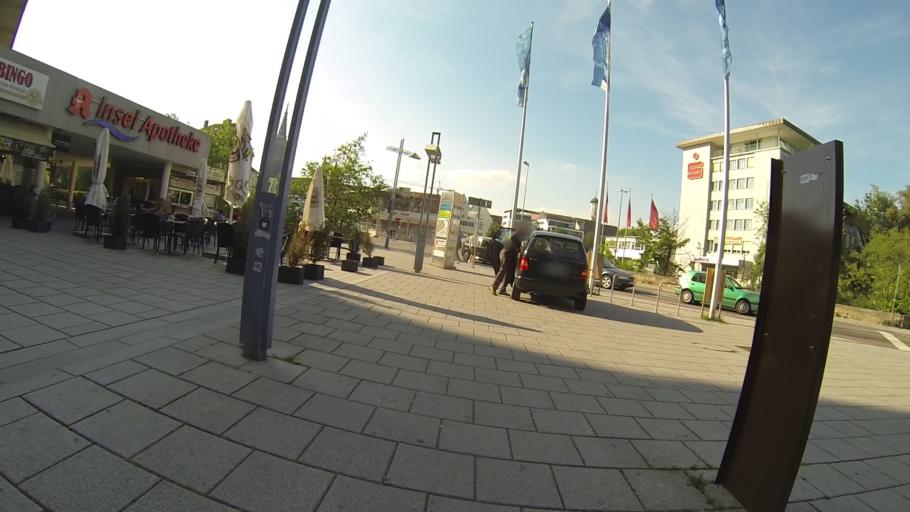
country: DE
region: Baden-Wuerttemberg
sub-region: Tuebingen Region
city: Ulm
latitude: 48.3948
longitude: 9.9973
